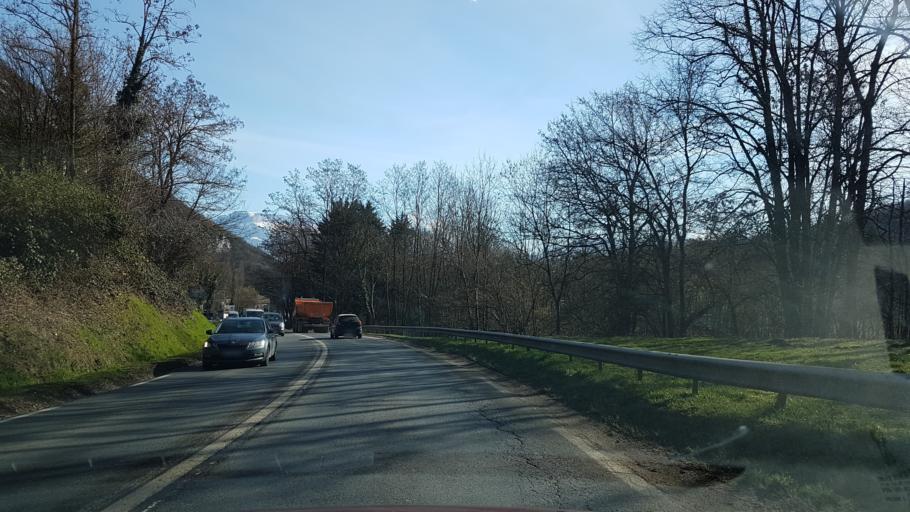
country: FR
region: Rhone-Alpes
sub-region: Departement de la Haute-Savoie
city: Sillingy
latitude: 45.9434
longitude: 6.0557
